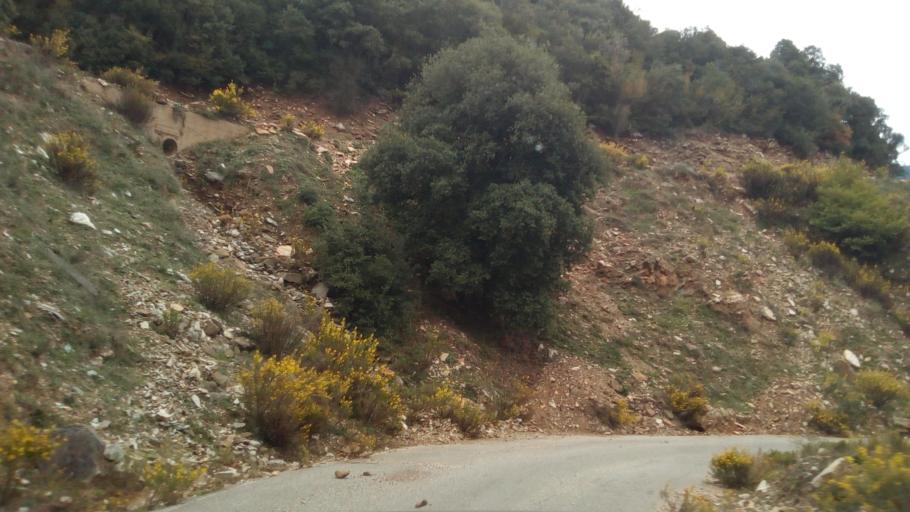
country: GR
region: West Greece
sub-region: Nomos Aitolias kai Akarnanias
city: Thermo
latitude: 38.6033
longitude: 21.8420
